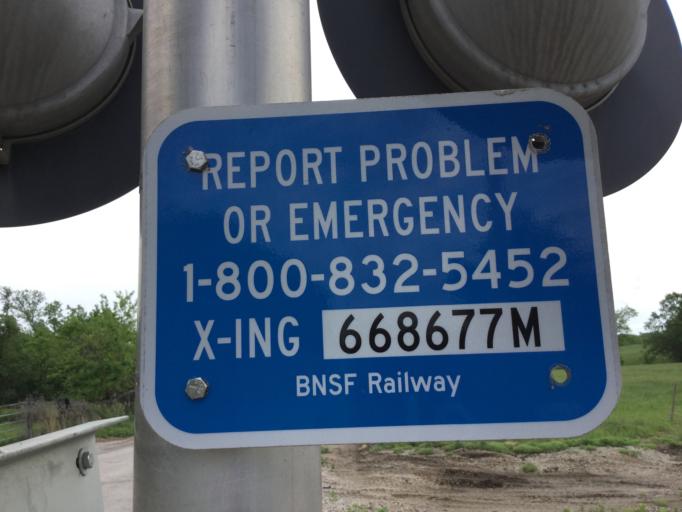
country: US
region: Kansas
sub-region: Linn County
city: Pleasanton
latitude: 38.1244
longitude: -94.6864
